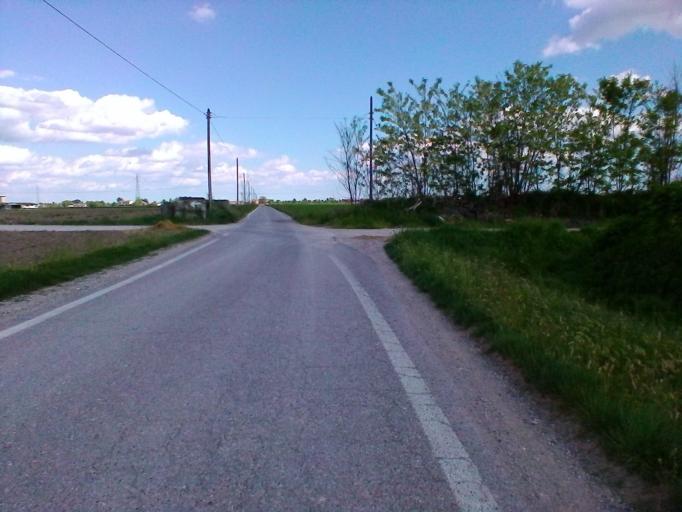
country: IT
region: Veneto
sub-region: Provincia di Verona
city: Mozzecane
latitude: 45.2961
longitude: 10.8325
